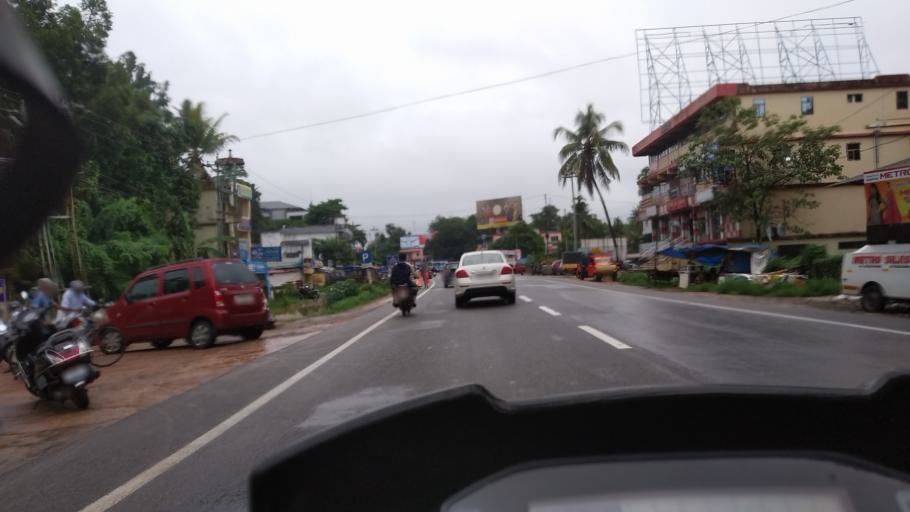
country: IN
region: Kerala
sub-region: Alappuzha
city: Mavelikara
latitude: 9.2772
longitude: 76.4598
